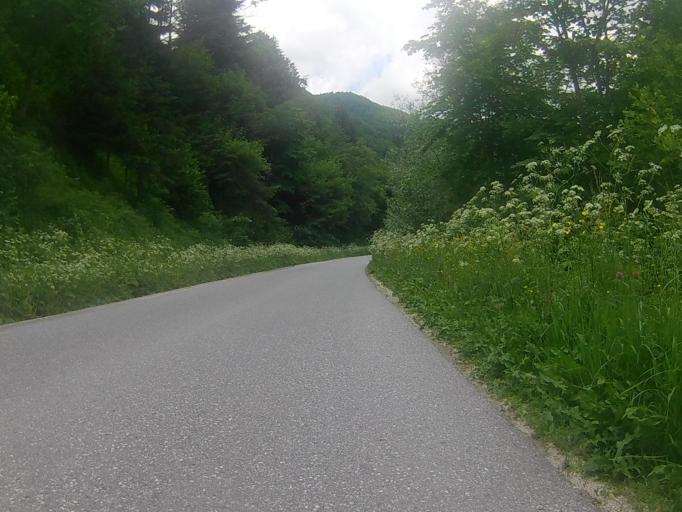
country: SI
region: Maribor
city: Bresternica
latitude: 46.5904
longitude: 15.5572
